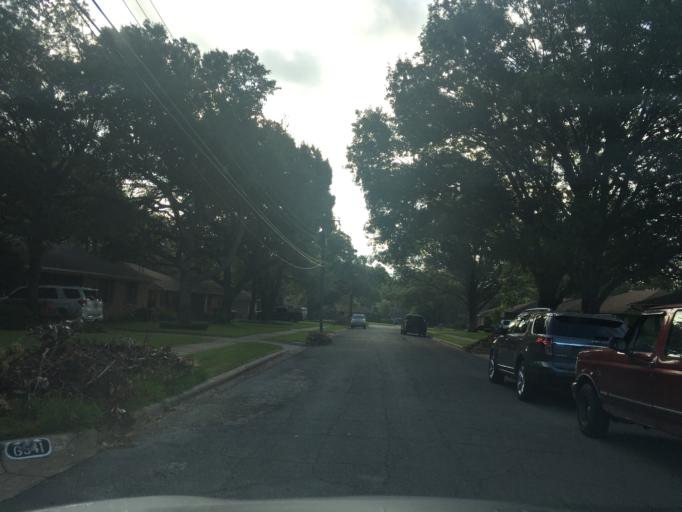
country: US
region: Texas
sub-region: Dallas County
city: Highland Park
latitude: 32.8475
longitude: -96.7488
